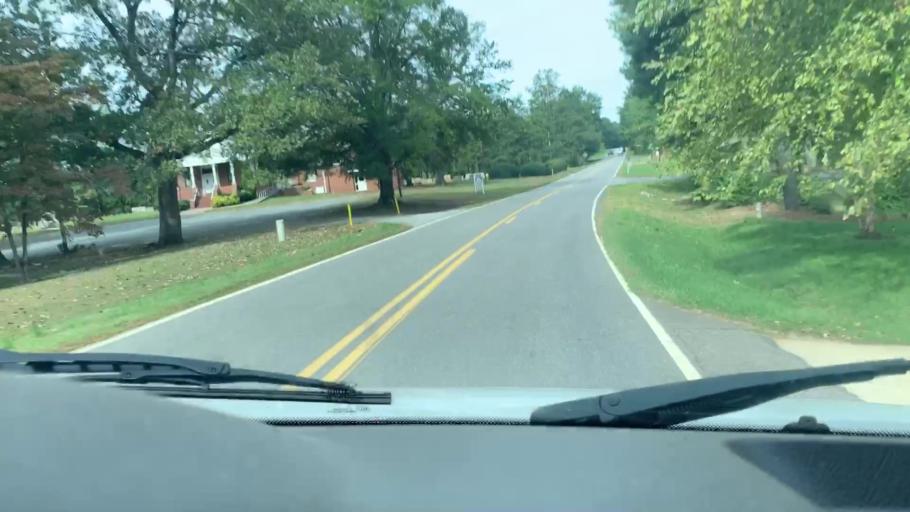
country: US
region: North Carolina
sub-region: Catawba County
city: Lake Norman of Catawba
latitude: 35.5659
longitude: -80.9295
